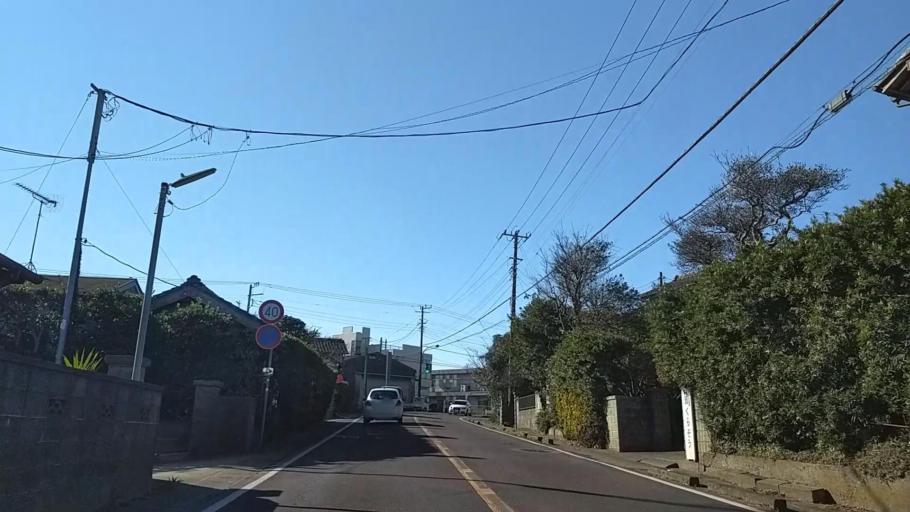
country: JP
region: Chiba
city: Hasaki
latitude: 35.7097
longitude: 140.7464
